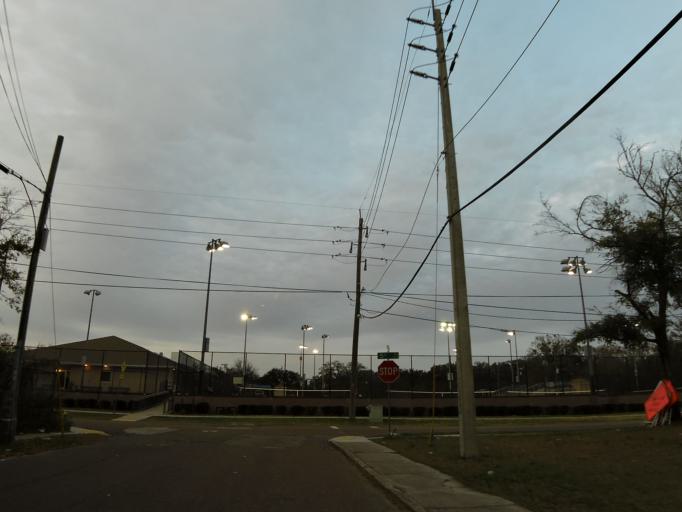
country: US
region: Florida
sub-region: Duval County
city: Jacksonville
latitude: 30.3427
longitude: -81.6708
